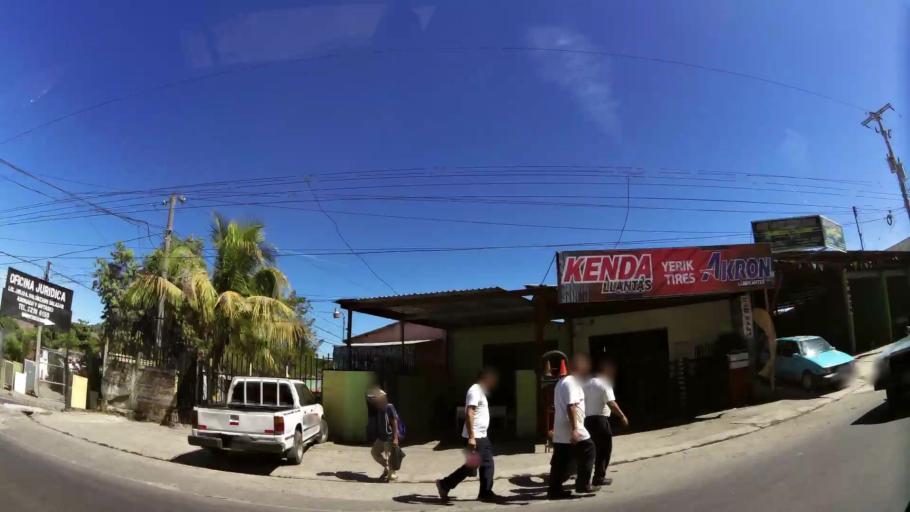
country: SV
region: San Salvador
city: Apopa
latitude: 13.7993
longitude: -89.1810
